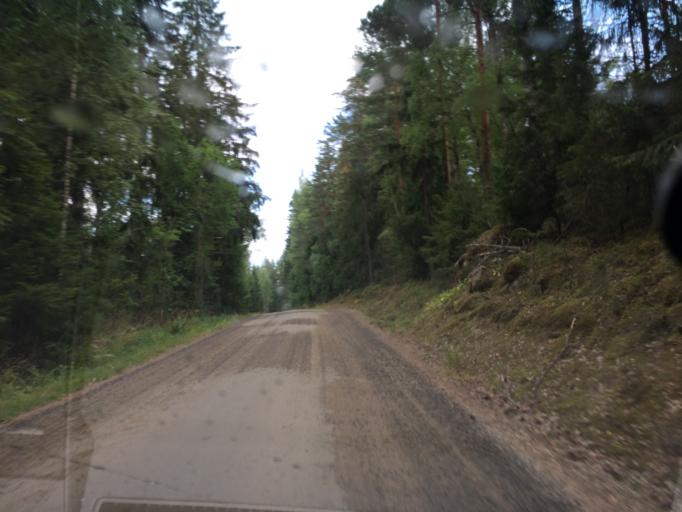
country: FI
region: Pirkanmaa
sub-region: Tampere
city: Luopioinen
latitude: 61.2701
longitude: 24.6777
